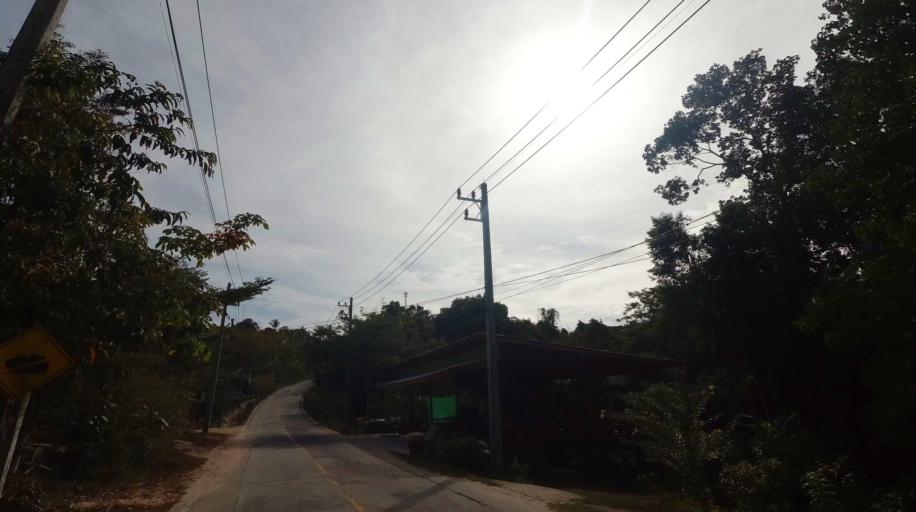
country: TH
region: Trat
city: Ko Kut
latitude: 11.6180
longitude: 102.5441
